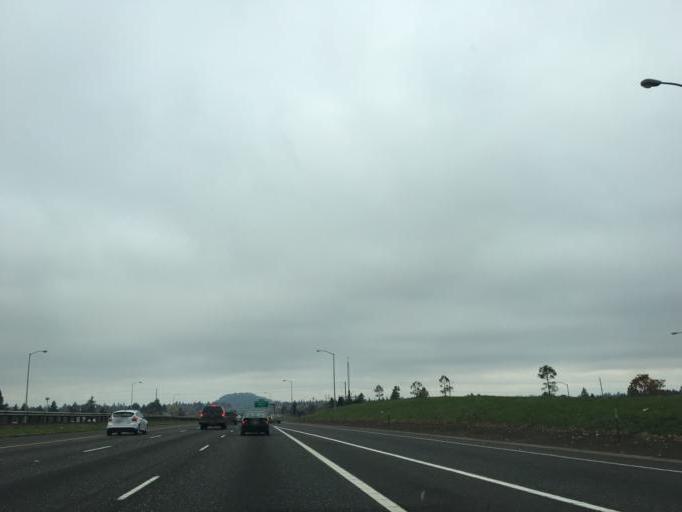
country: US
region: Oregon
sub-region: Multnomah County
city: Lents
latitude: 45.5015
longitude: -122.5650
